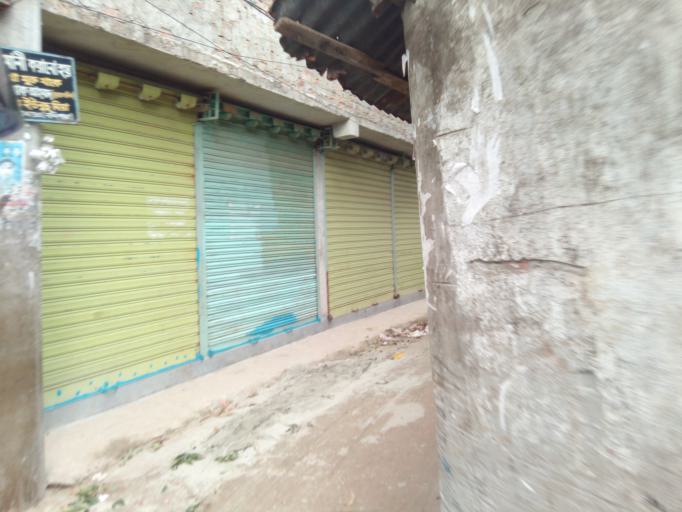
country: BD
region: Dhaka
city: Paltan
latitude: 23.7479
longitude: 90.4484
